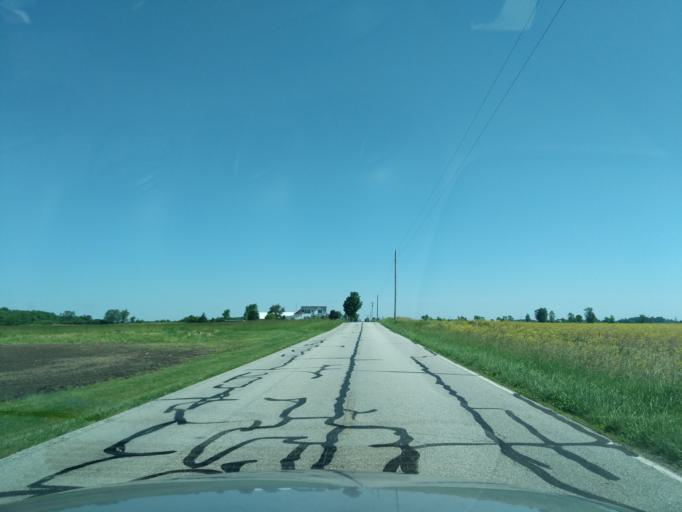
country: US
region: Indiana
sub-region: Huntington County
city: Warren
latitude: 40.6765
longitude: -85.5067
